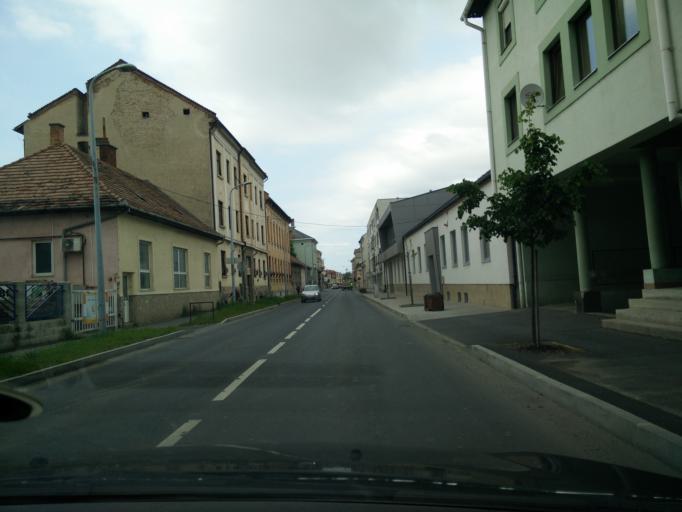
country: HU
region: Zala
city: Zalaegerszeg
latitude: 46.8438
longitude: 16.8429
